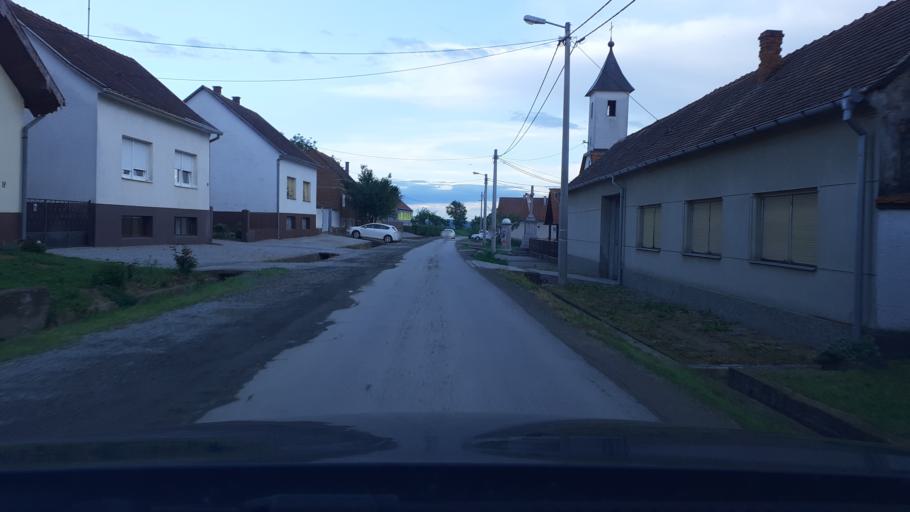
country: HR
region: Pozesko-Slavonska
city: Gradac
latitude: 45.3369
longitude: 17.7959
